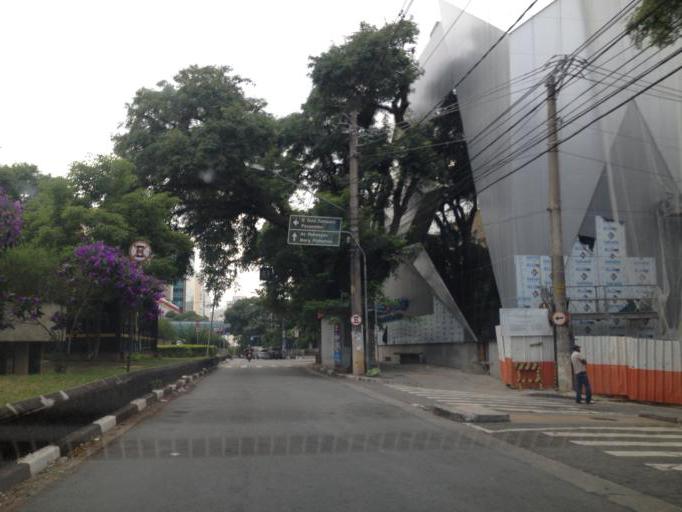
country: BR
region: Sao Paulo
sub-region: Sao Paulo
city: Sao Paulo
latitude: -23.5563
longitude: -46.6709
